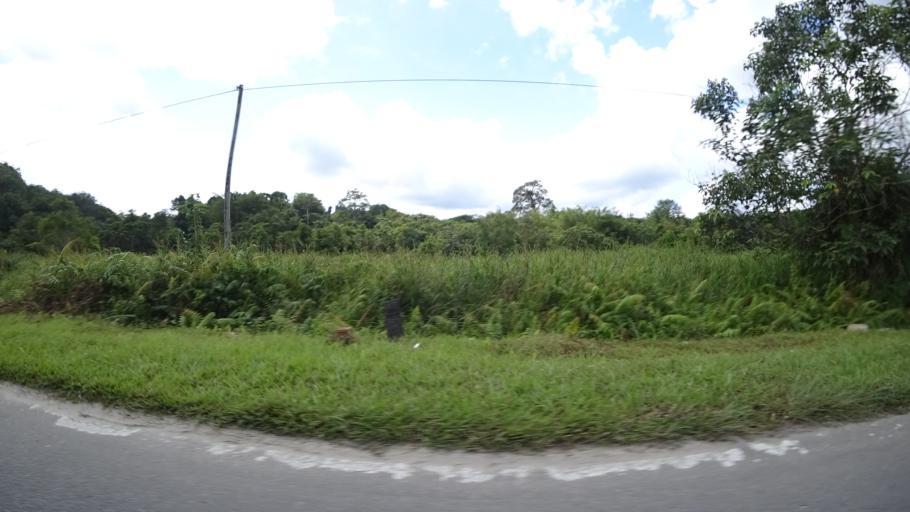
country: BN
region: Tutong
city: Tutong
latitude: 4.6992
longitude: 114.8024
